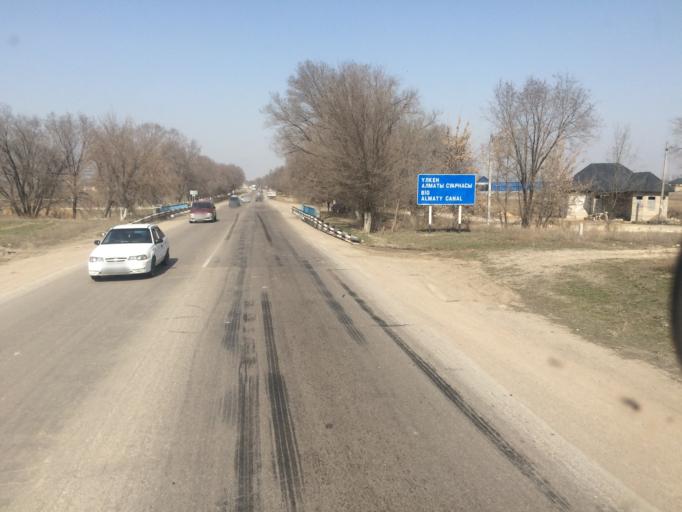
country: KZ
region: Almaty Oblysy
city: Burunday
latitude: 43.3262
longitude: 76.6625
